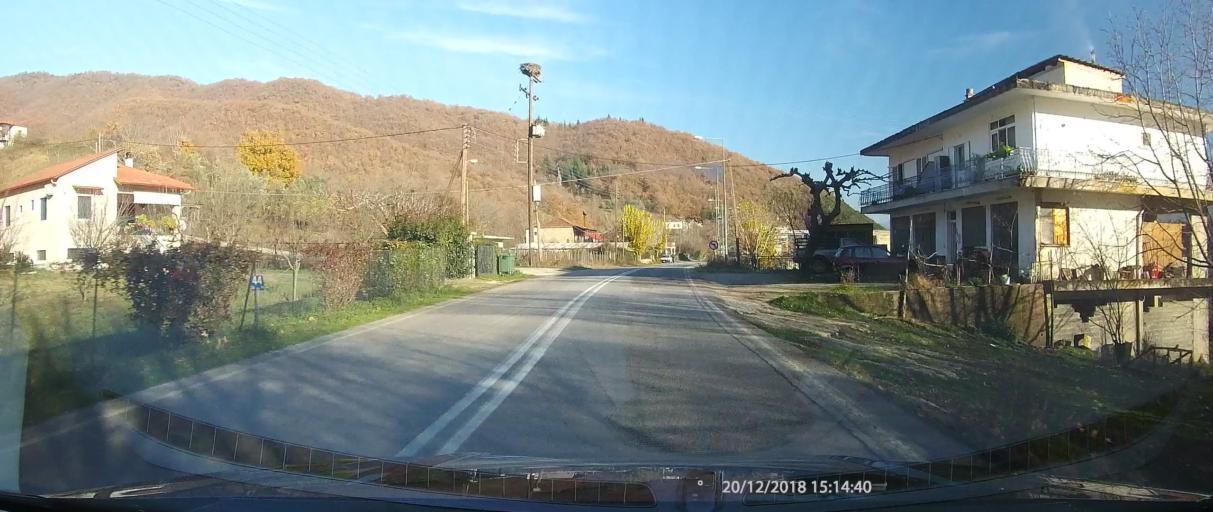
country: GR
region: Central Greece
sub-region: Nomos Fthiotidos
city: Makrakomi
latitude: 38.9319
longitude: 21.9808
